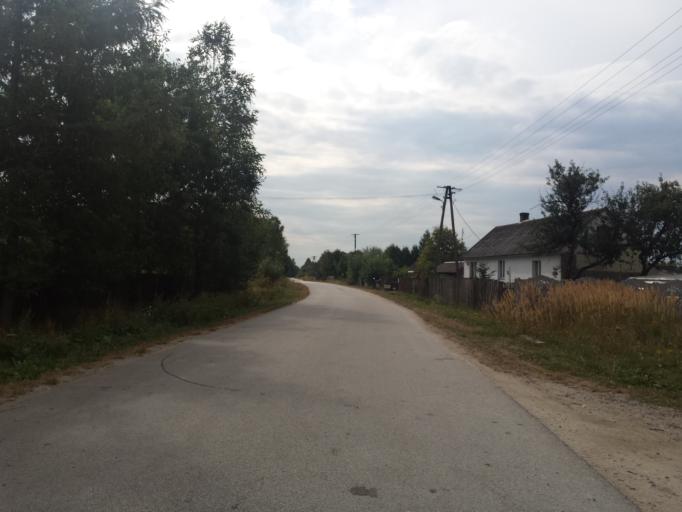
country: PL
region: Swietokrzyskie
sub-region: Powiat kielecki
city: Rakow
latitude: 50.6678
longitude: 21.1272
